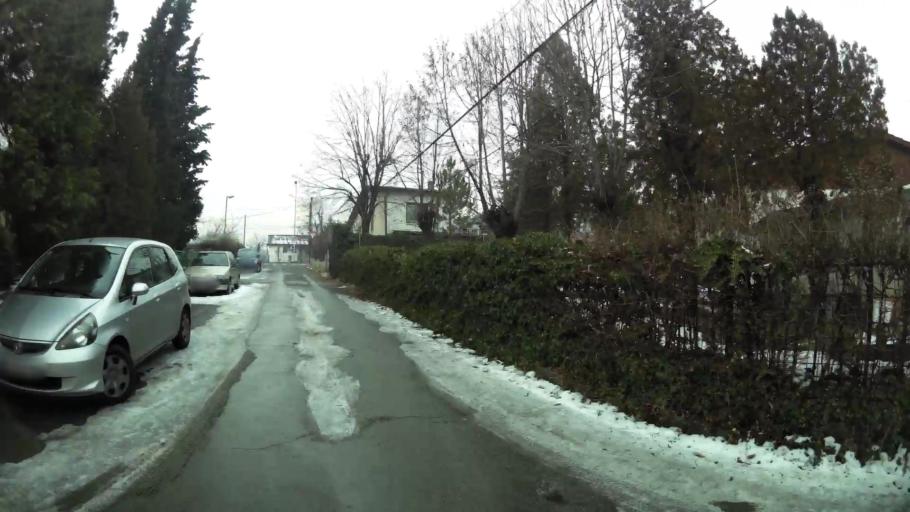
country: MK
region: Cair
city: Cair
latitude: 42.0138
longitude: 21.4580
